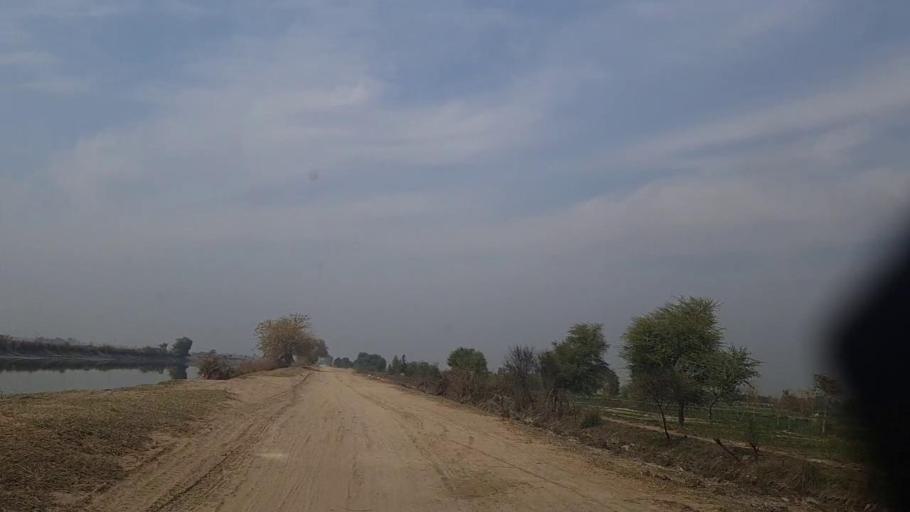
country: PK
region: Sindh
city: Daur
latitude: 26.3251
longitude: 68.1949
